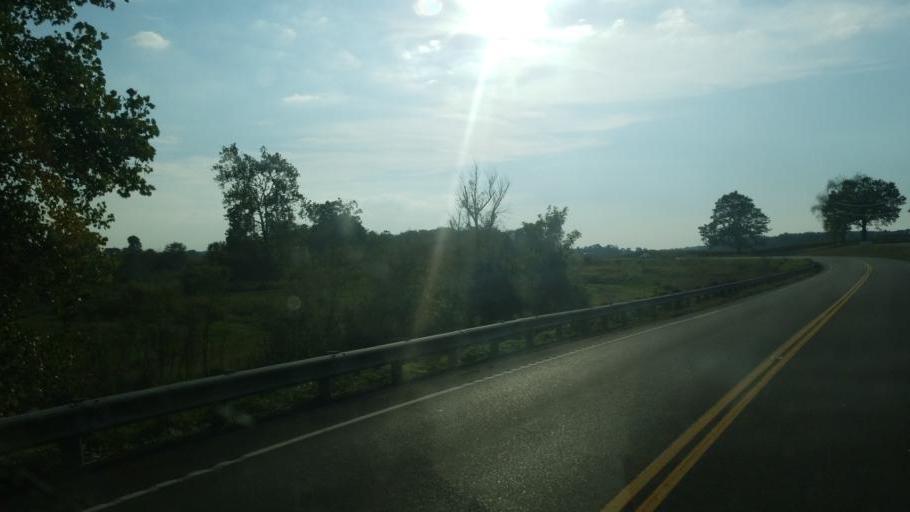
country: US
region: Ohio
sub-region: Knox County
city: Fredericktown
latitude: 40.4659
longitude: -82.6110
